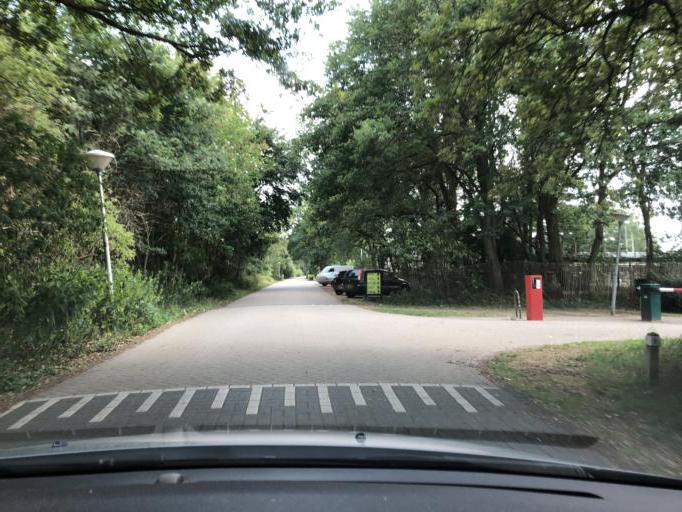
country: NL
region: Drenthe
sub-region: Gemeente De Wolden
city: Ruinen
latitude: 52.6121
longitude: 6.3708
